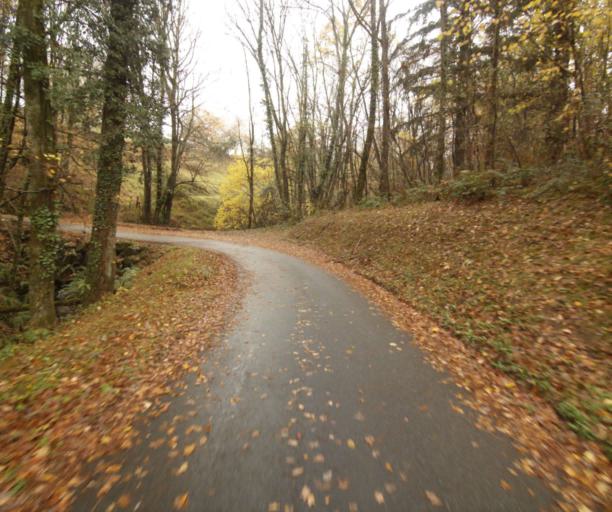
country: FR
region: Limousin
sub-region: Departement de la Correze
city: Sainte-Fereole
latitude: 45.1834
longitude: 1.6296
